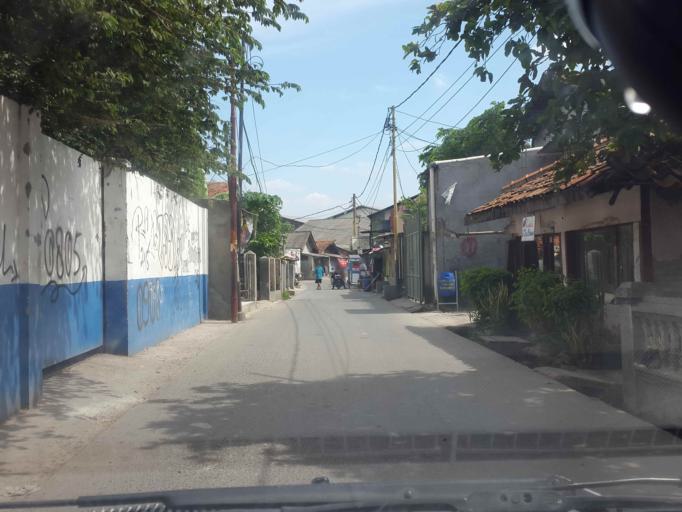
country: ID
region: Banten
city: Tangerang
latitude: -6.1527
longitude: 106.6815
